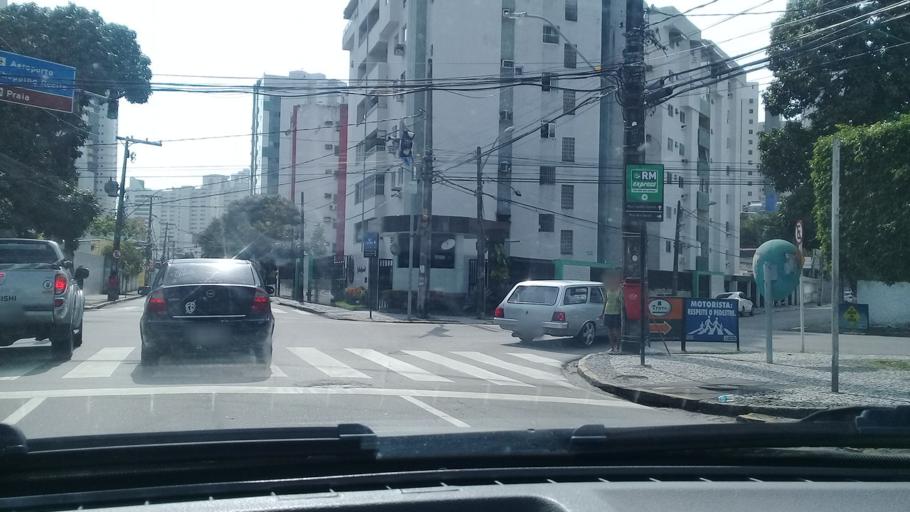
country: BR
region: Pernambuco
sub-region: Recife
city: Recife
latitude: -8.1349
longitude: -34.9064
